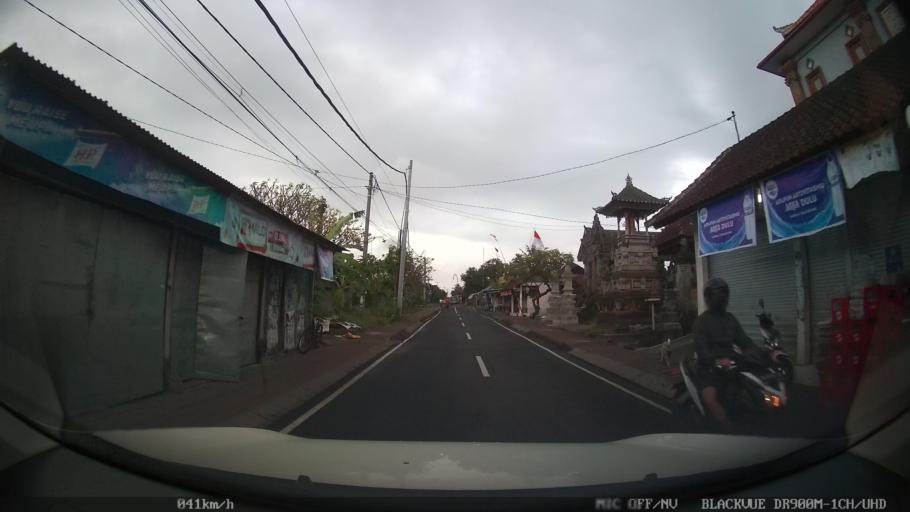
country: ID
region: Bali
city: Banjar Pasekan
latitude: -8.6104
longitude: 115.2873
